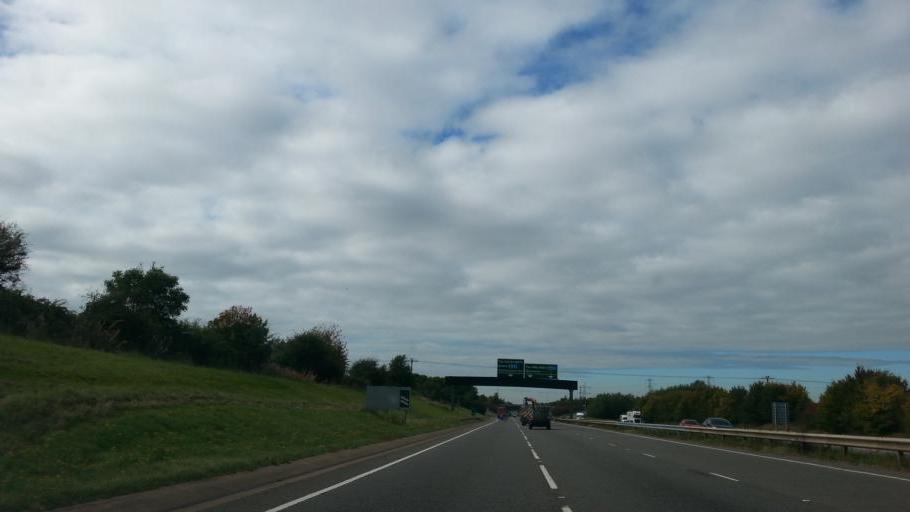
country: GB
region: England
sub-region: Gloucestershire
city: Churchdown
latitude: 51.8553
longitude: -2.1601
